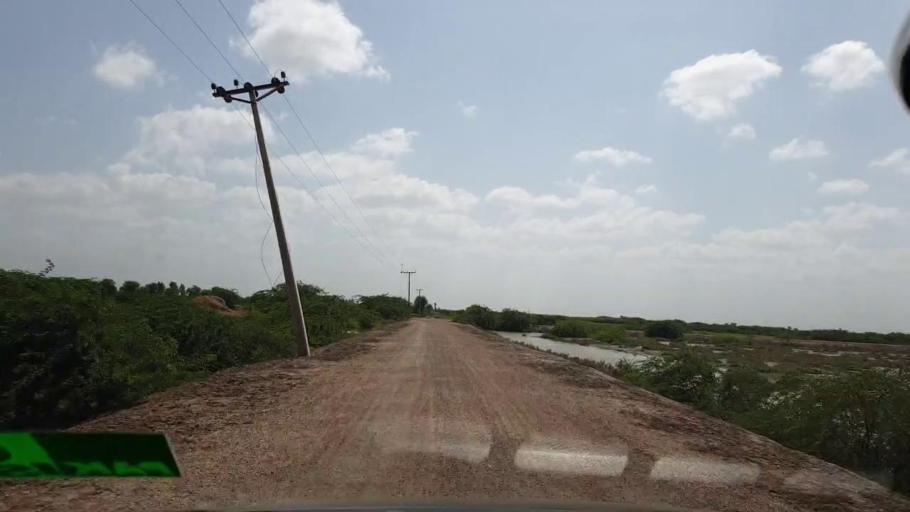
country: PK
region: Sindh
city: Kadhan
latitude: 24.5999
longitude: 69.1852
